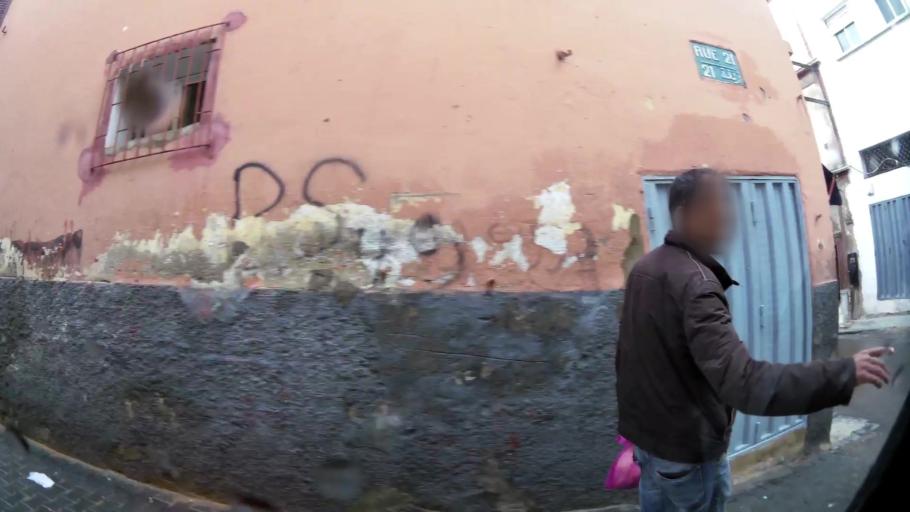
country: MA
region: Grand Casablanca
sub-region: Casablanca
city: Casablanca
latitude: 33.5735
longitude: -7.5947
